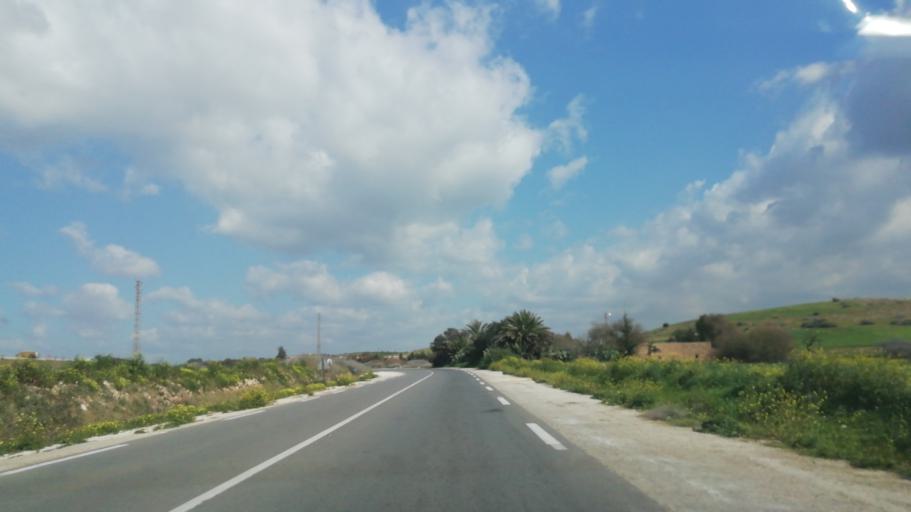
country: DZ
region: Mostaganem
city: Mostaganem
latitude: 35.7007
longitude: 0.2509
